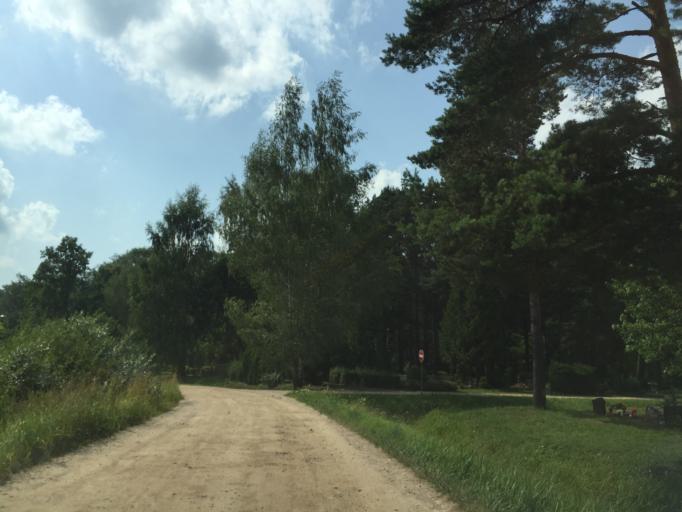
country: LV
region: Jelgava
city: Jelgava
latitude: 56.6723
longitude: 23.7461
